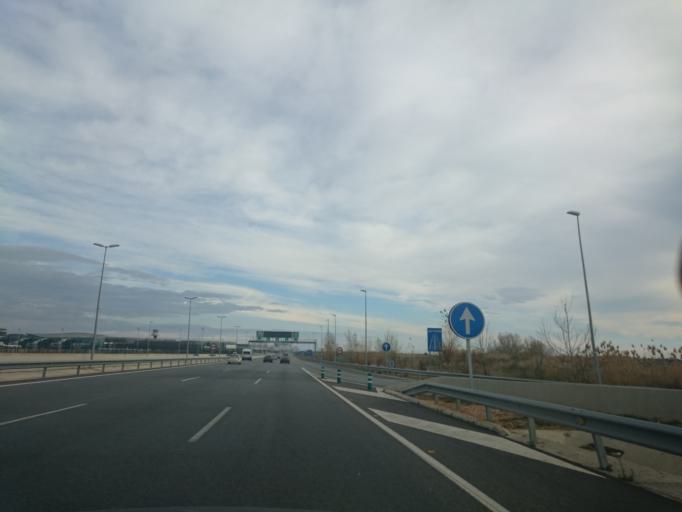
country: ES
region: Catalonia
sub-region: Provincia de Barcelona
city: Viladecans
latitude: 41.2917
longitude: 2.0584
